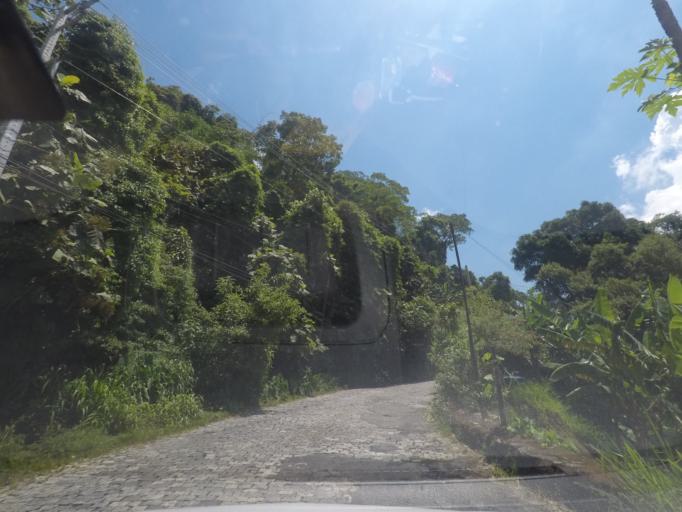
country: BR
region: Rio de Janeiro
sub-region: Petropolis
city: Petropolis
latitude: -22.5383
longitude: -43.1773
